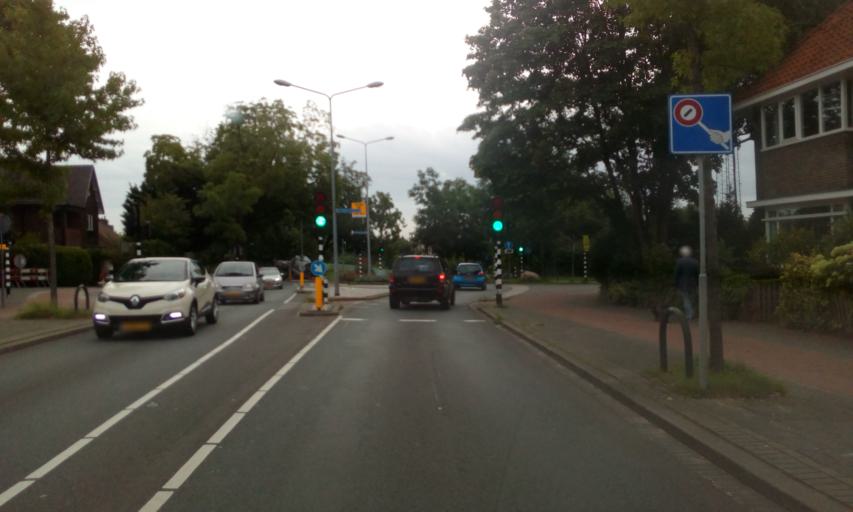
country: NL
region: North Holland
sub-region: Gemeente Hilversum
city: Hilversum
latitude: 52.2113
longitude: 5.1732
